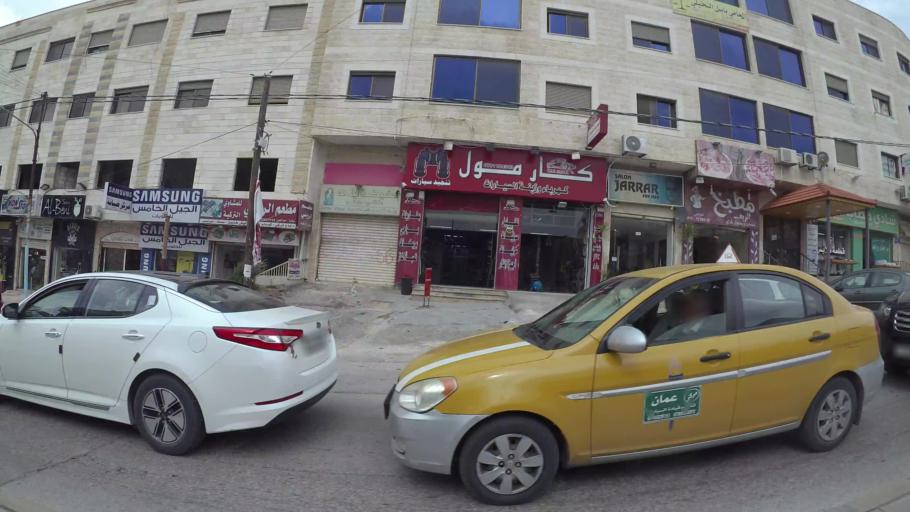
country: JO
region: Amman
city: Umm as Summaq
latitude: 31.8876
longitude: 35.8534
